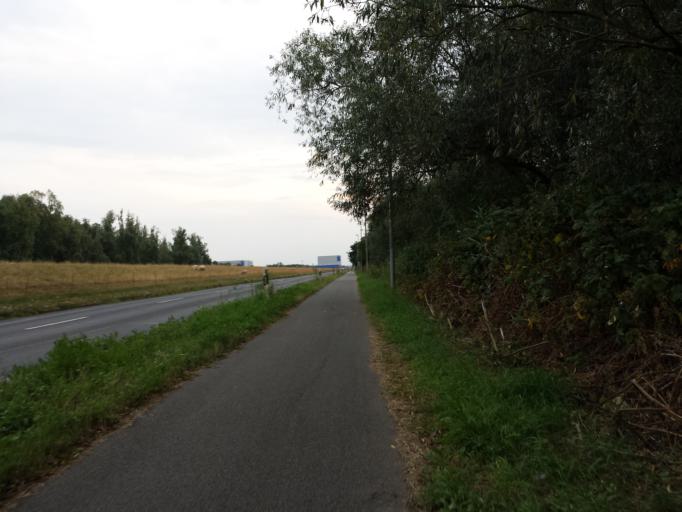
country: DE
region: Lower Saxony
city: Stuhr
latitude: 53.1045
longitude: 8.7233
